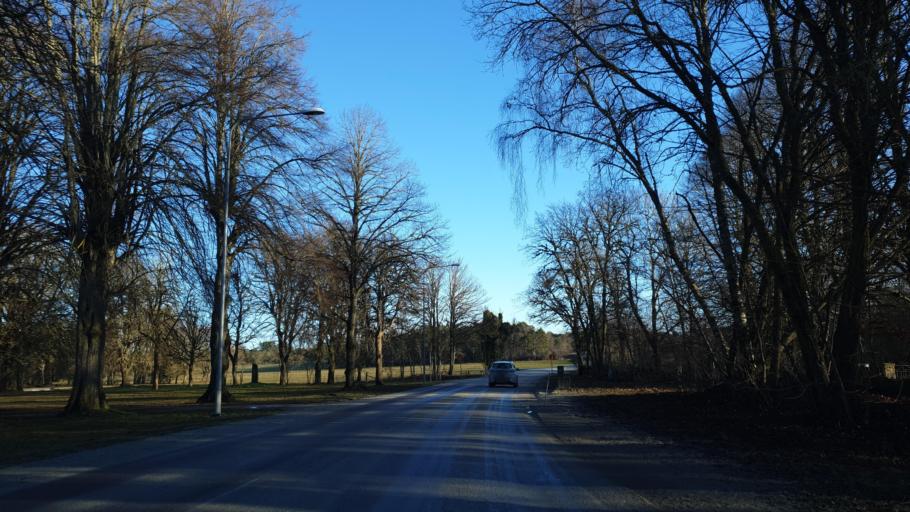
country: SE
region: Gotland
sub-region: Gotland
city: Slite
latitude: 57.7857
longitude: 18.7930
